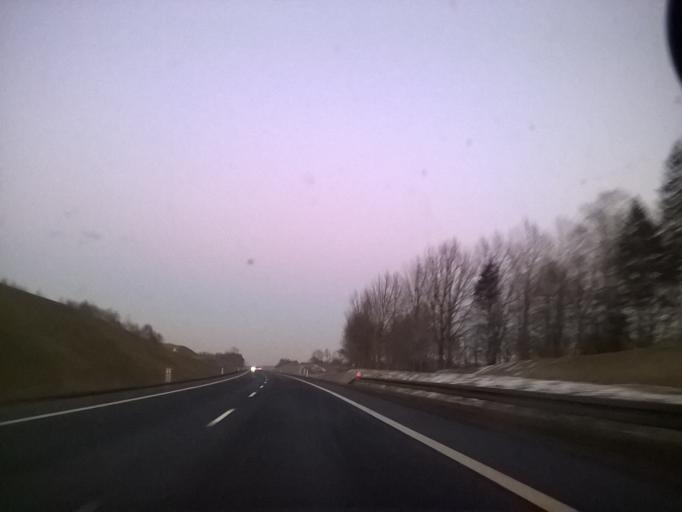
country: PL
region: Warmian-Masurian Voivodeship
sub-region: Powiat olsztynski
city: Biskupiec
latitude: 53.8302
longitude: 20.8903
